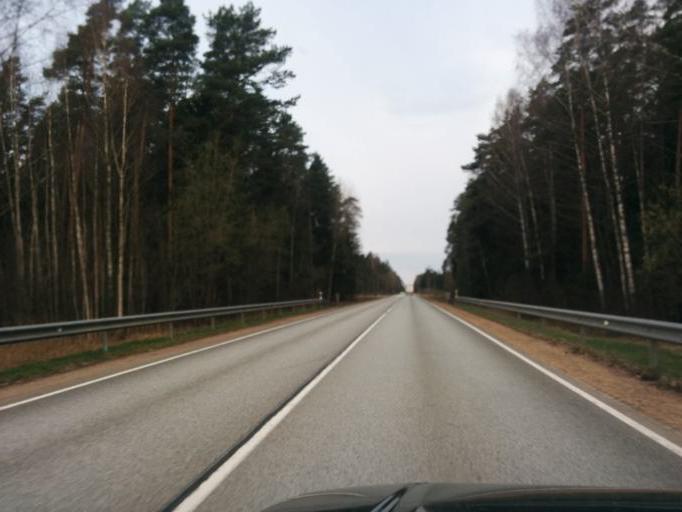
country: LV
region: Kekava
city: Kekava
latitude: 56.8114
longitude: 24.1635
